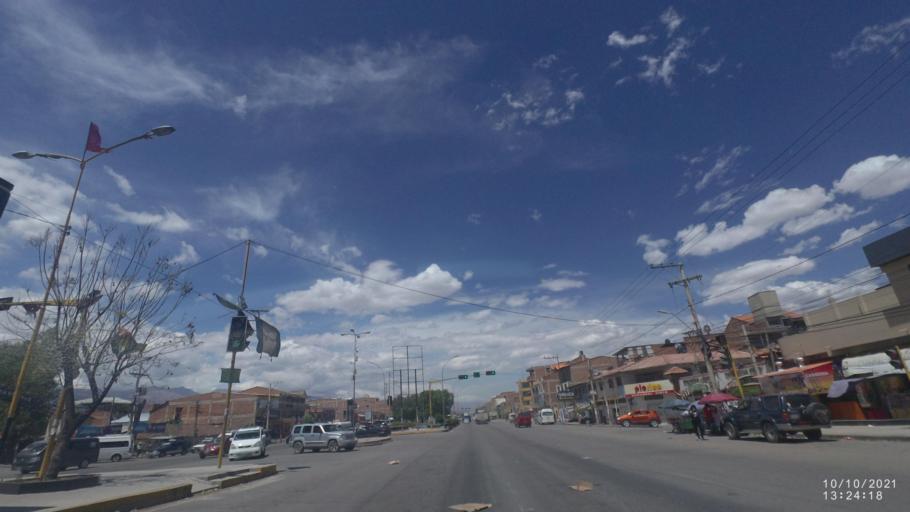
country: BO
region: Cochabamba
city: Sipe Sipe
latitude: -17.3961
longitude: -66.3168
